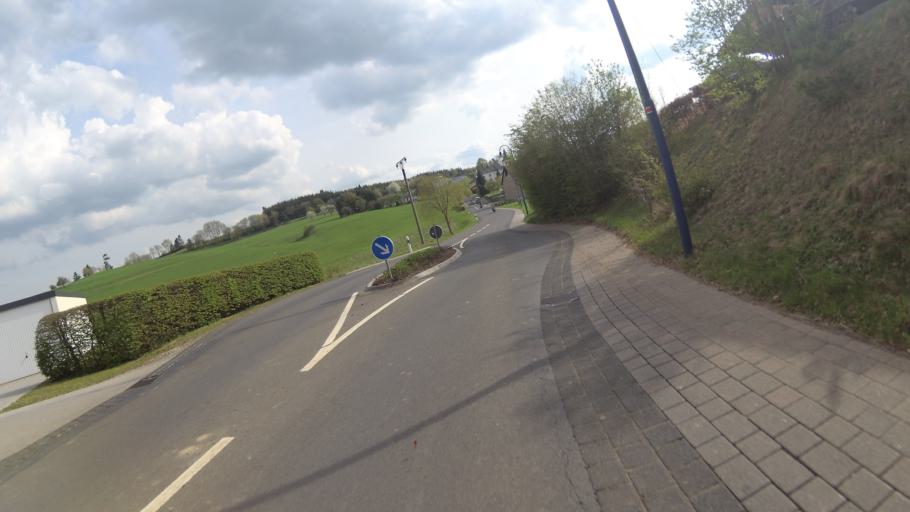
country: DE
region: Rheinland-Pfalz
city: Welcherath
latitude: 50.3123
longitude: 6.9609
